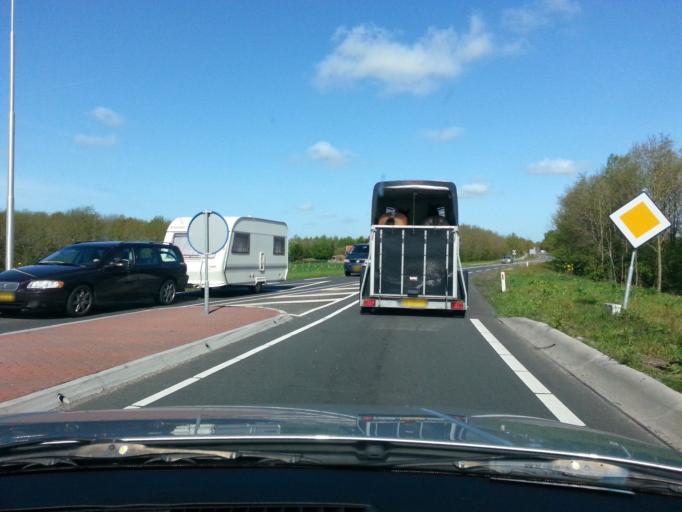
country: NL
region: Friesland
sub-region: Gemeente Smallingerland
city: Drachtstercompagnie
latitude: 53.1305
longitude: 6.1839
